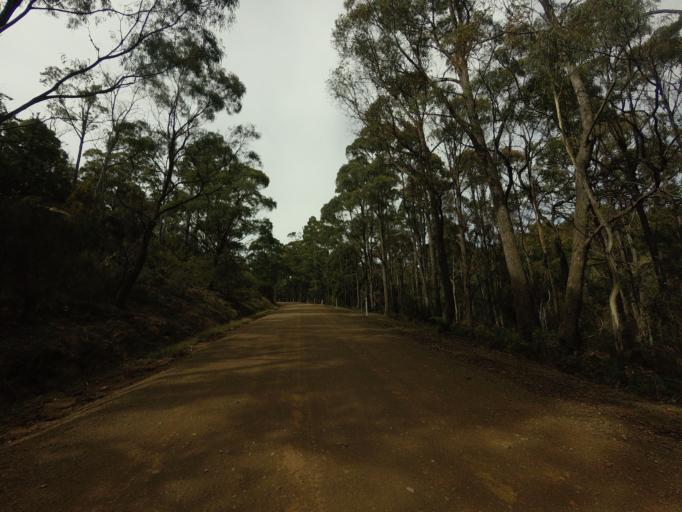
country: AU
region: Tasmania
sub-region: Sorell
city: Sorell
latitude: -42.4813
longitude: 147.6144
